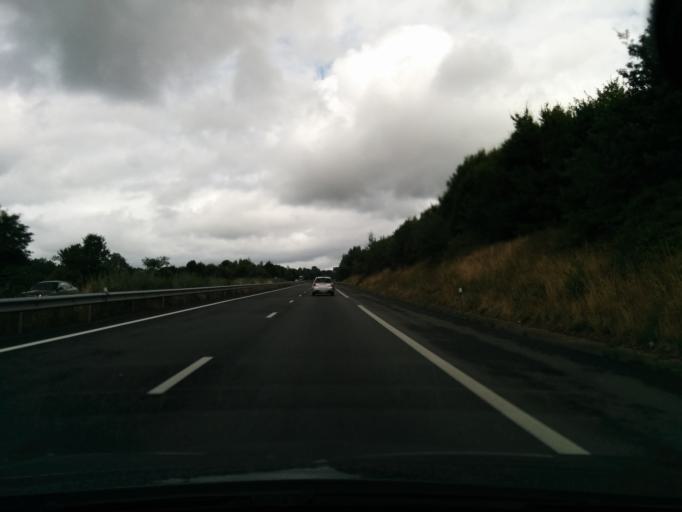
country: FR
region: Limousin
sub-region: Departement de la Correze
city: Vigeois
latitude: 45.4239
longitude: 1.5158
